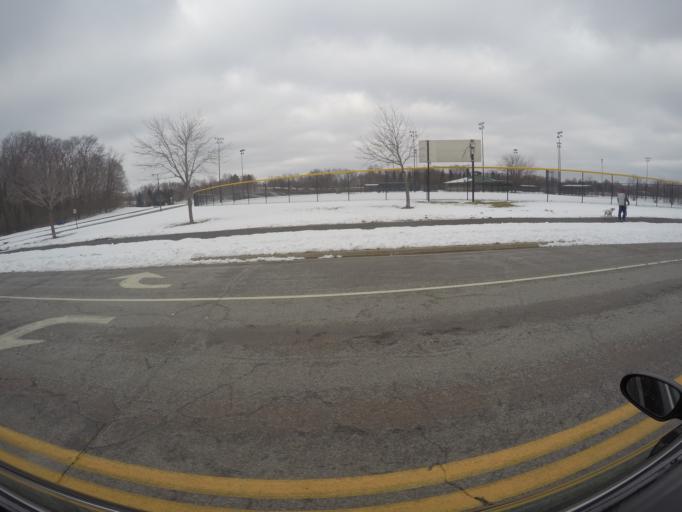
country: US
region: Minnesota
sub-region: Hennepin County
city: Eden Prairie
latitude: 44.8526
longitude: -93.4927
